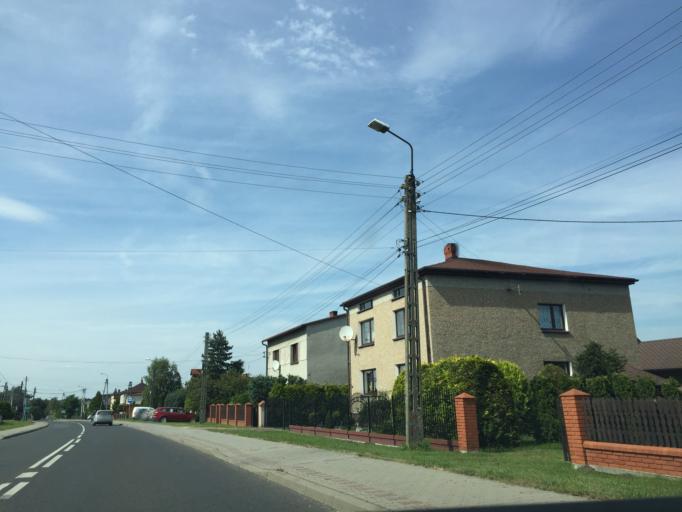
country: PL
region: Silesian Voivodeship
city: Gorzyczki
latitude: 49.9530
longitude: 18.4022
